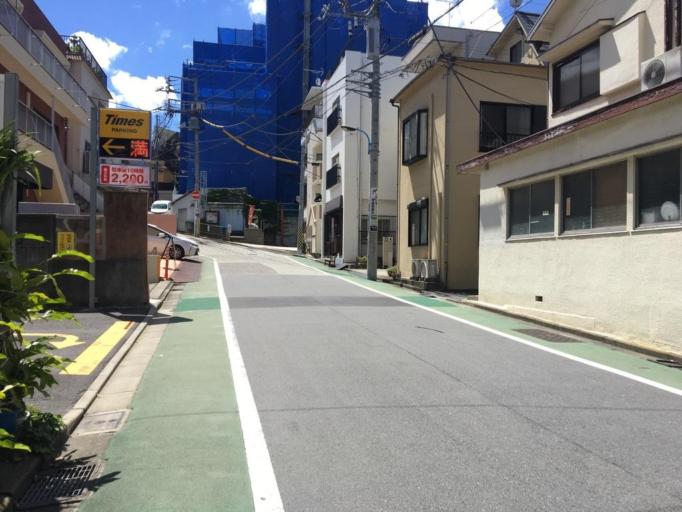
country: JP
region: Tokyo
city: Tokyo
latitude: 35.7058
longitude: 139.7354
